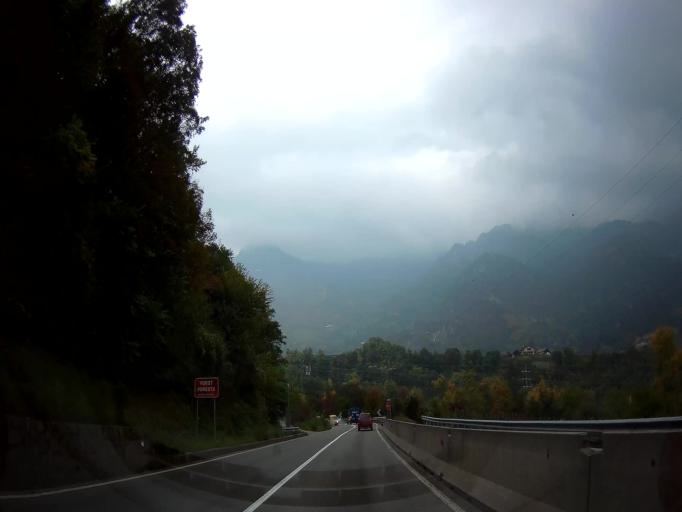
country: IT
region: Trentino-Alto Adige
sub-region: Bolzano
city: Parcines
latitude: 46.6798
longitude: 11.0987
